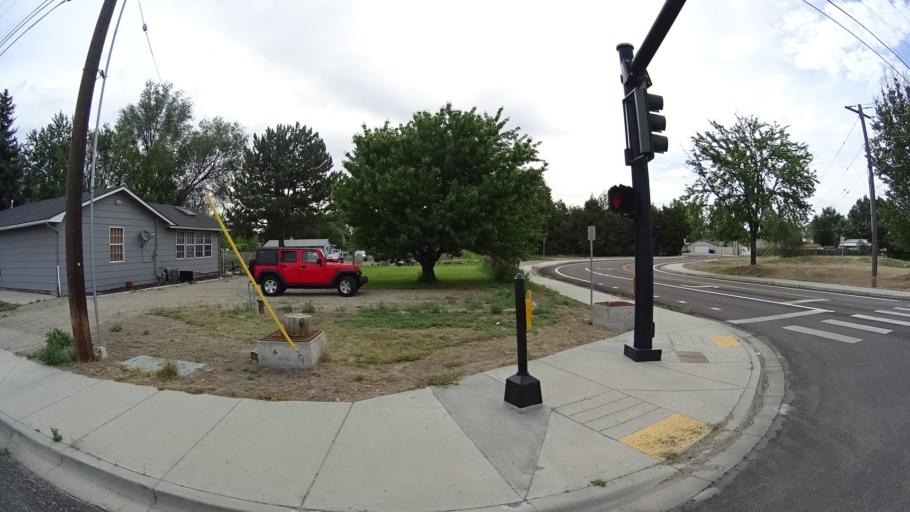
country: US
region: Idaho
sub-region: Ada County
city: Meridian
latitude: 43.5963
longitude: -116.3745
